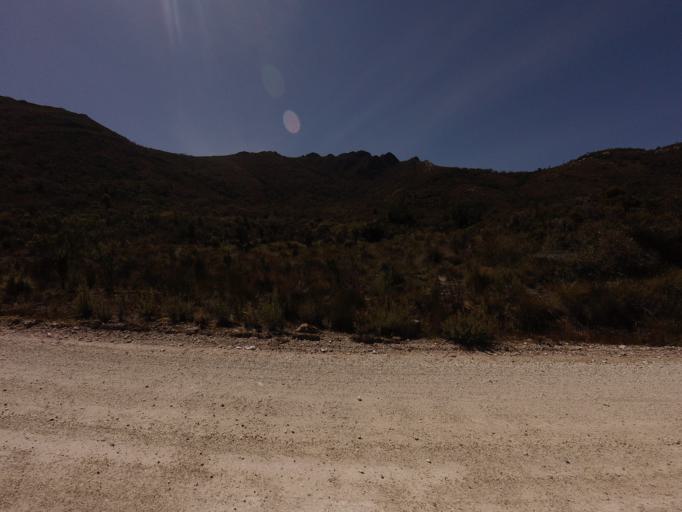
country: AU
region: Tasmania
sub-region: Huon Valley
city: Geeveston
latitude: -42.9366
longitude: 146.3474
